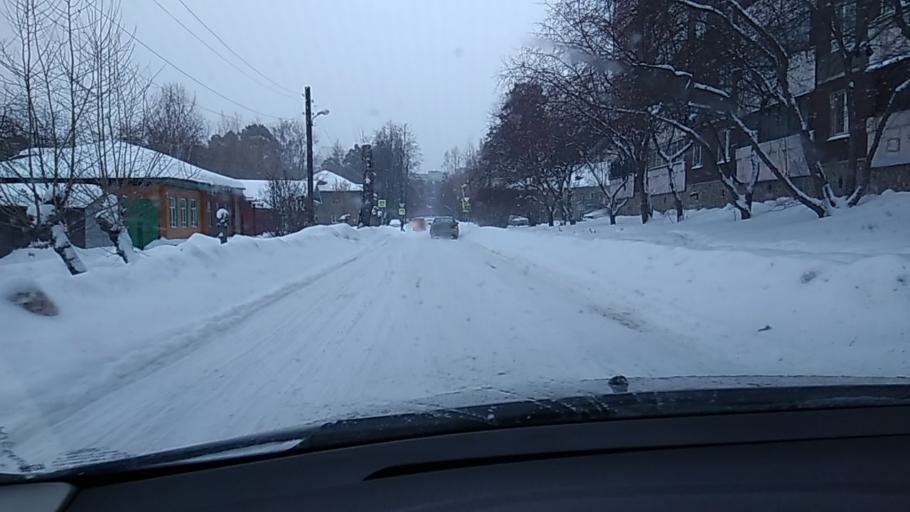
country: RU
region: Sverdlovsk
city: Sovkhoznyy
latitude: 56.8193
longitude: 60.5466
